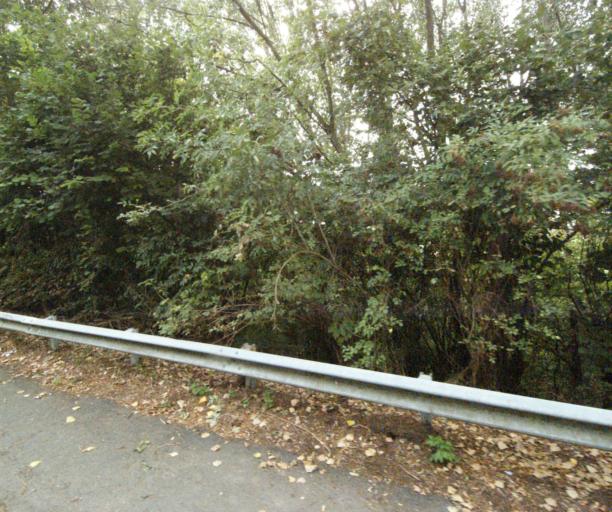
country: FR
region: Nord-Pas-de-Calais
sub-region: Departement du Nord
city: Sainghin-en-Melantois
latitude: 50.5998
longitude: 3.1657
